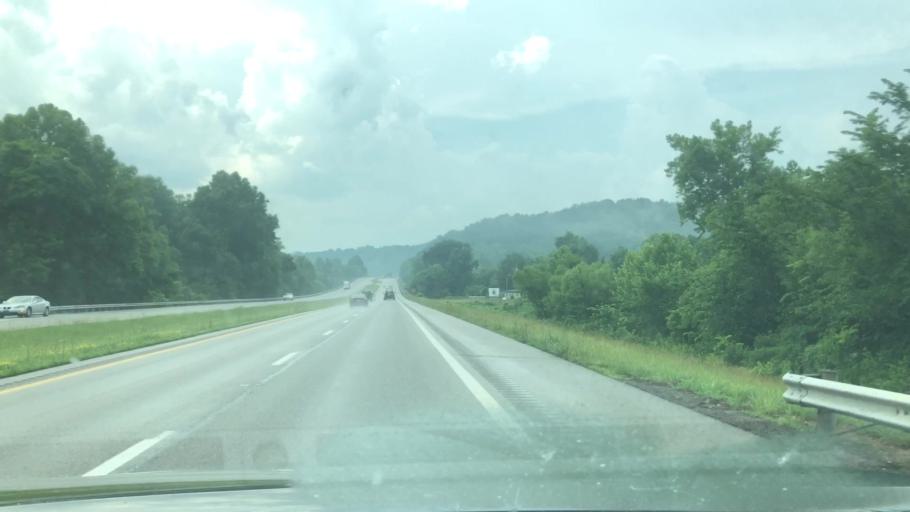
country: US
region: Ohio
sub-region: Jackson County
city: Jackson
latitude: 39.1375
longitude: -82.7189
